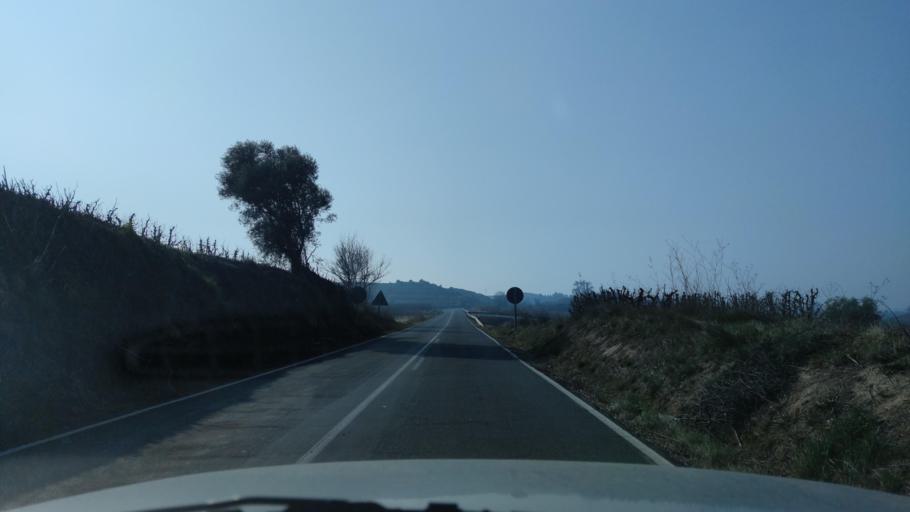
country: ES
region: Catalonia
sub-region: Provincia de Lleida
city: Sunyer
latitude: 41.5675
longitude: 0.5916
